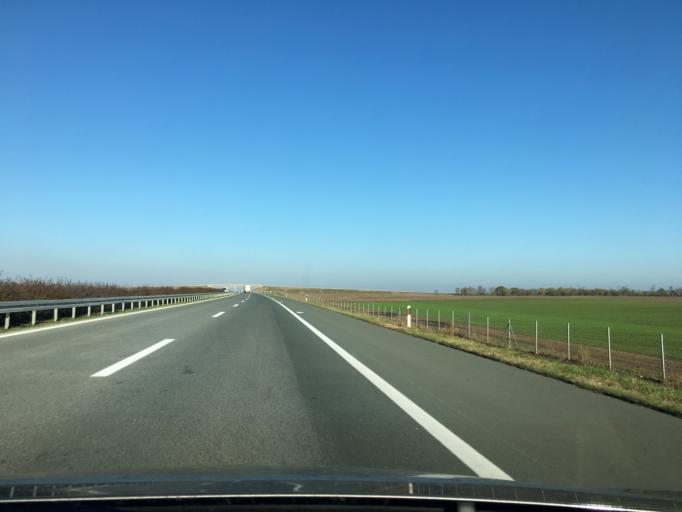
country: RS
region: Autonomna Pokrajina Vojvodina
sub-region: Severnobacki Okrug
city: Mali Igos
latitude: 45.6916
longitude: 19.7253
